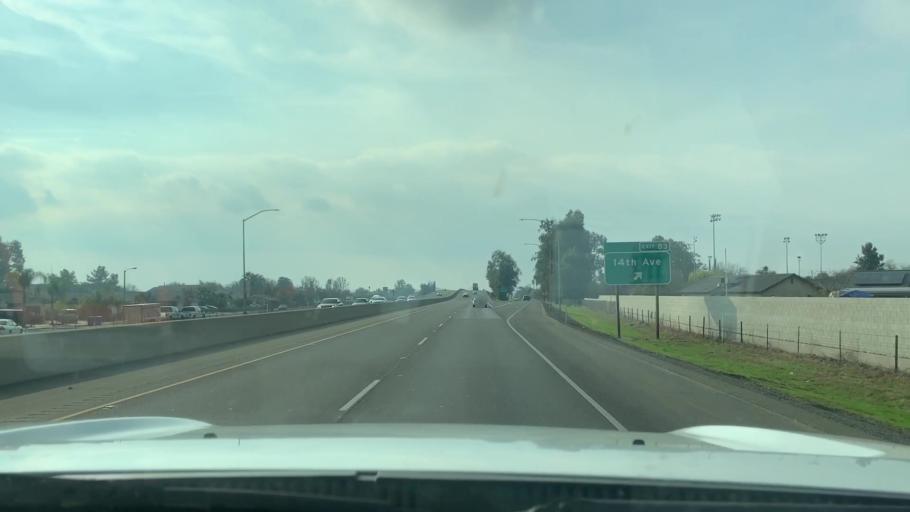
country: US
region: California
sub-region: Kings County
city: Armona
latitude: 36.3108
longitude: -119.7036
